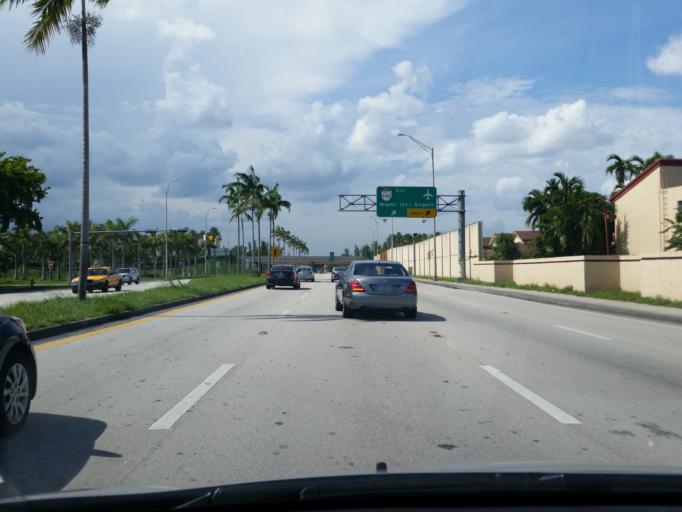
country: US
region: Florida
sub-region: Miami-Dade County
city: Sweetwater
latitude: 25.7772
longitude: -80.3693
